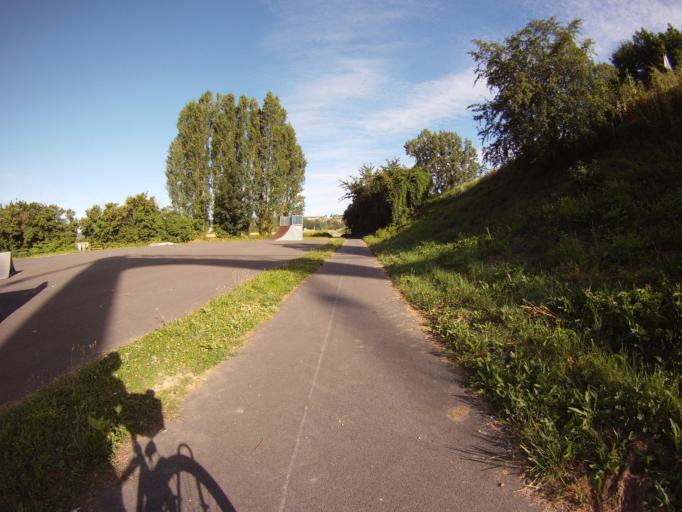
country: FR
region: Champagne-Ardenne
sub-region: Departement de la Marne
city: Dormans
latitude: 49.0757
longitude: 3.6362
